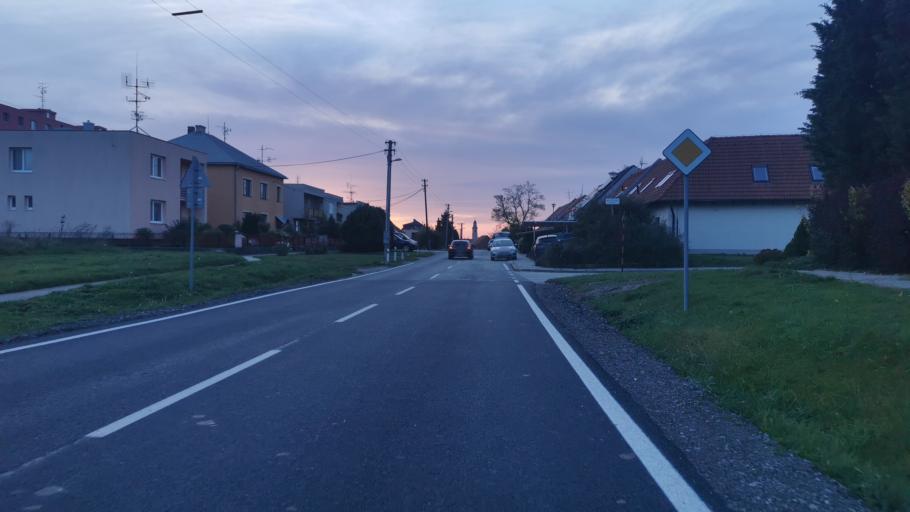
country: SK
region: Trnavsky
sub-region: Okres Skalica
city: Skalica
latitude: 48.8477
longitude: 17.2414
